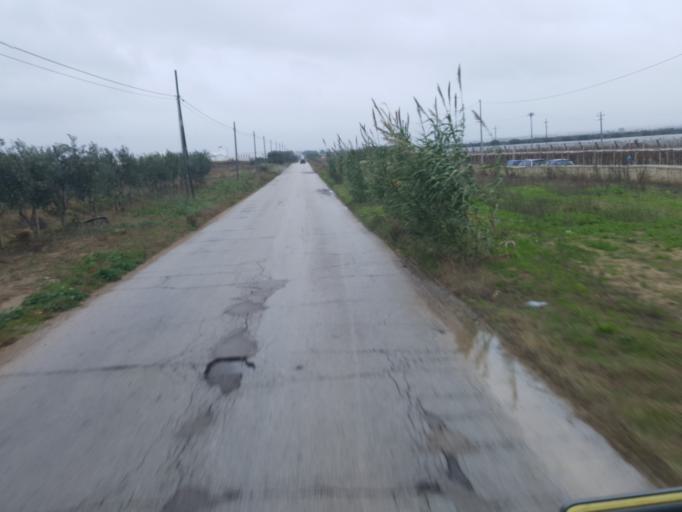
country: IT
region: Apulia
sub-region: Provincia di Taranto
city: Montemesola
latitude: 40.5464
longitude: 17.3643
